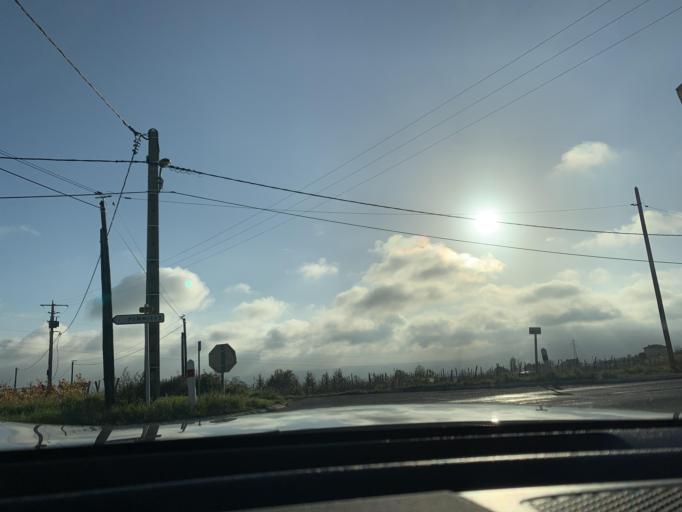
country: FR
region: Rhone-Alpes
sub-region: Departement du Rhone
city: Pommiers
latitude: 45.9442
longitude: 4.6900
